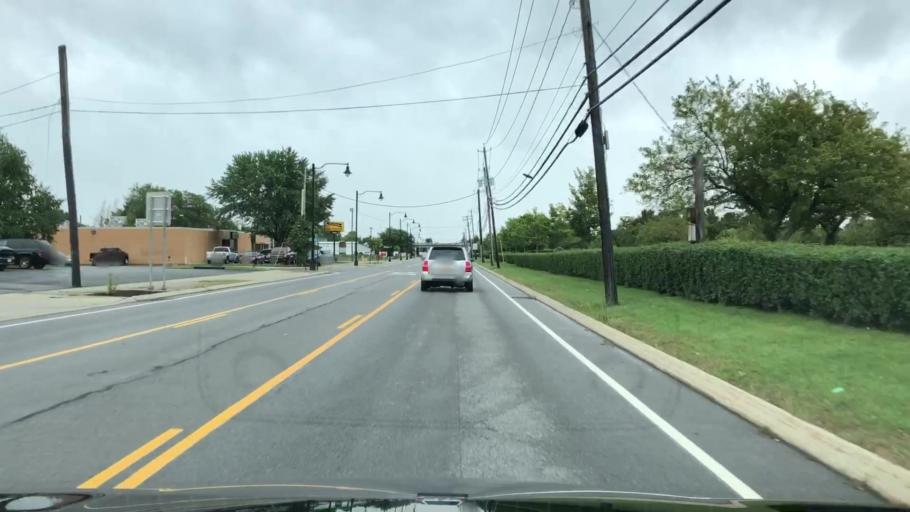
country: US
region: New York
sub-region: Erie County
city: Eggertsville
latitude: 42.9368
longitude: -78.7842
